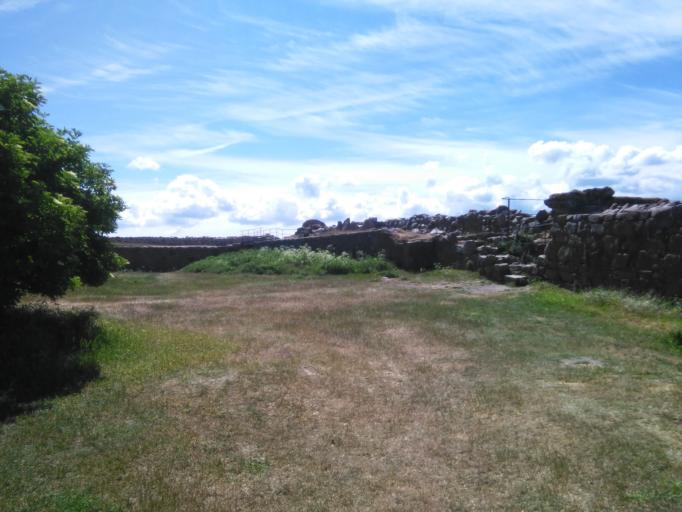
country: DK
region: Capital Region
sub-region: Bornholm Kommune
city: Ronne
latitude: 55.2705
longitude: 14.7545
